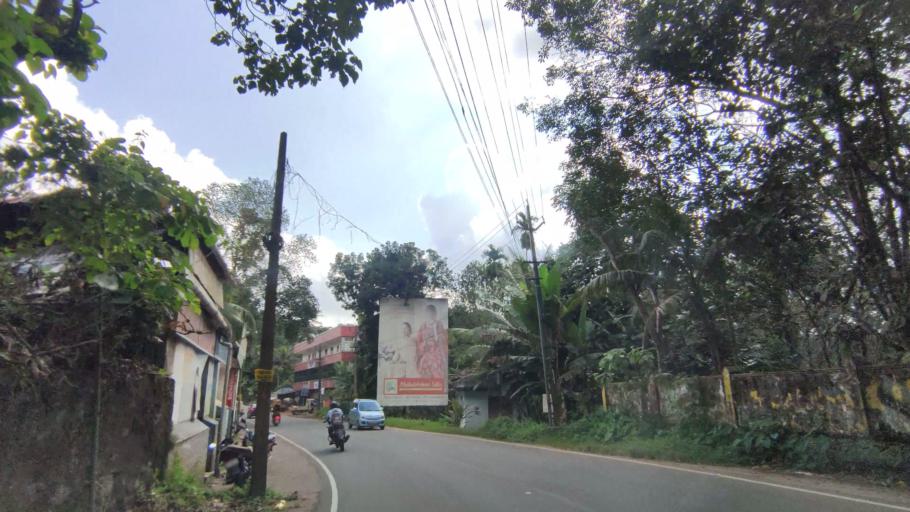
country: IN
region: Kerala
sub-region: Kottayam
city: Kottayam
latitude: 9.6756
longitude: 76.5406
